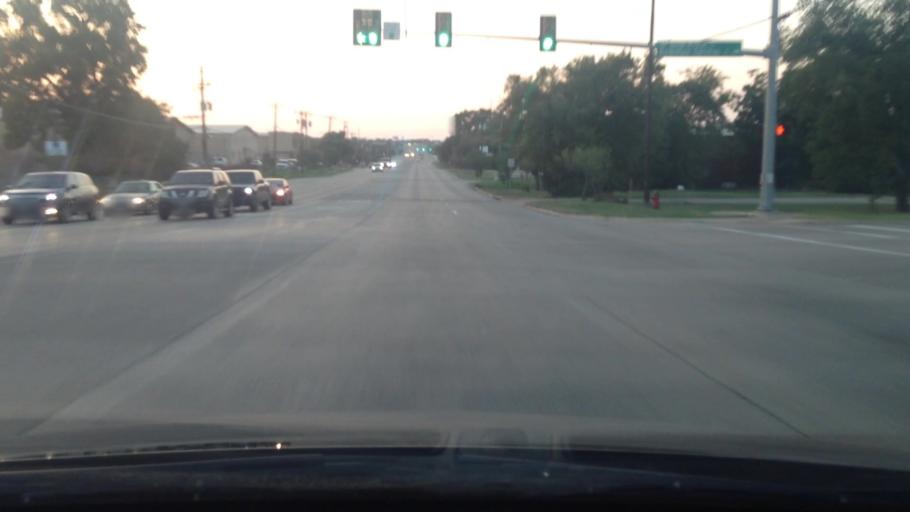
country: US
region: Texas
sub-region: Tarrant County
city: Kennedale
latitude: 32.6548
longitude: -97.2300
